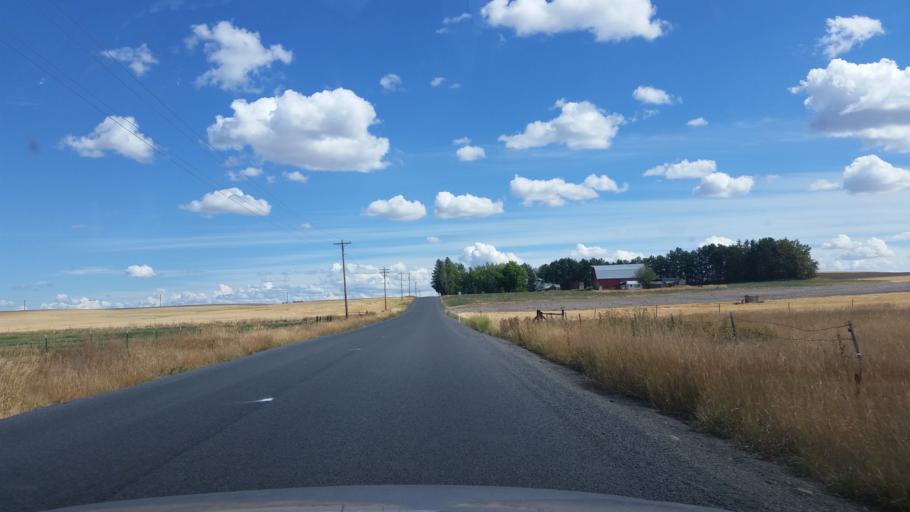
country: US
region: Washington
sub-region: Spokane County
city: Cheney
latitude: 47.5004
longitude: -117.6470
